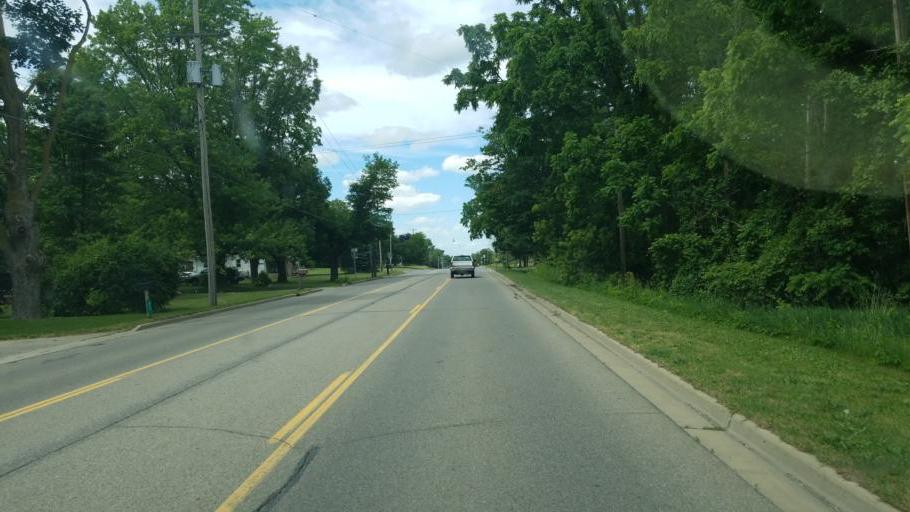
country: US
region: Michigan
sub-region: Eaton County
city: Charlotte
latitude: 42.5778
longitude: -84.8360
